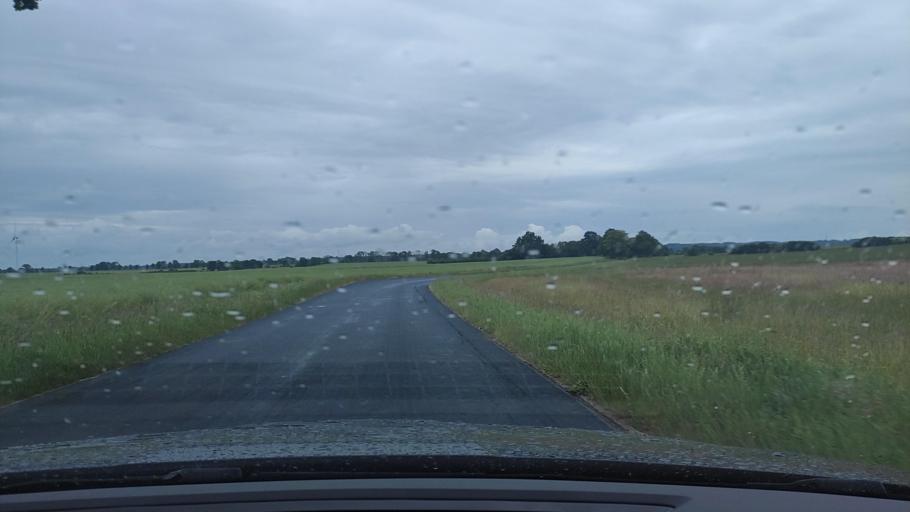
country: PL
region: West Pomeranian Voivodeship
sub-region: Powiat slawienski
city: Slawno
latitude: 54.5195
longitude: 16.5820
